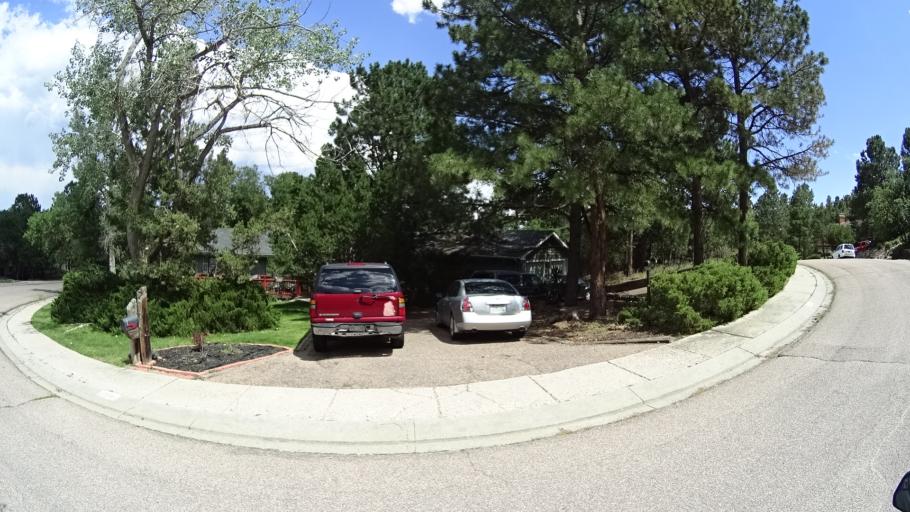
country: US
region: Colorado
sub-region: El Paso County
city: Air Force Academy
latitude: 38.9337
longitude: -104.8376
